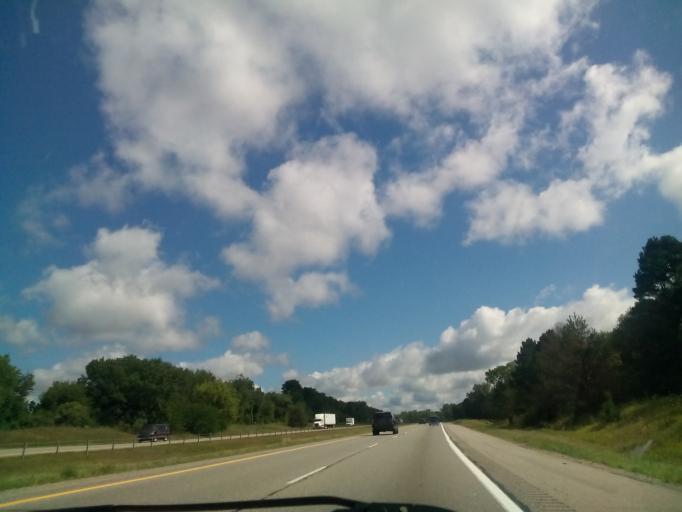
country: US
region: Michigan
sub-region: Livingston County
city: Brighton
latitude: 42.5535
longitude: -83.7468
